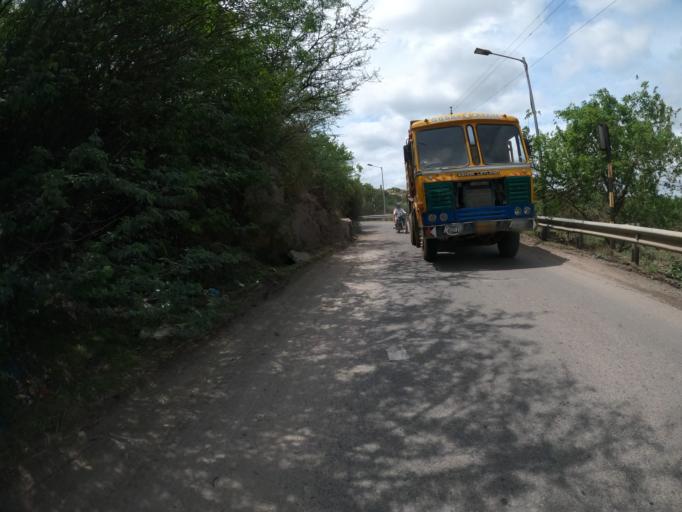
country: IN
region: Telangana
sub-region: Hyderabad
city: Hyderabad
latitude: 17.3171
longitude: 78.3714
